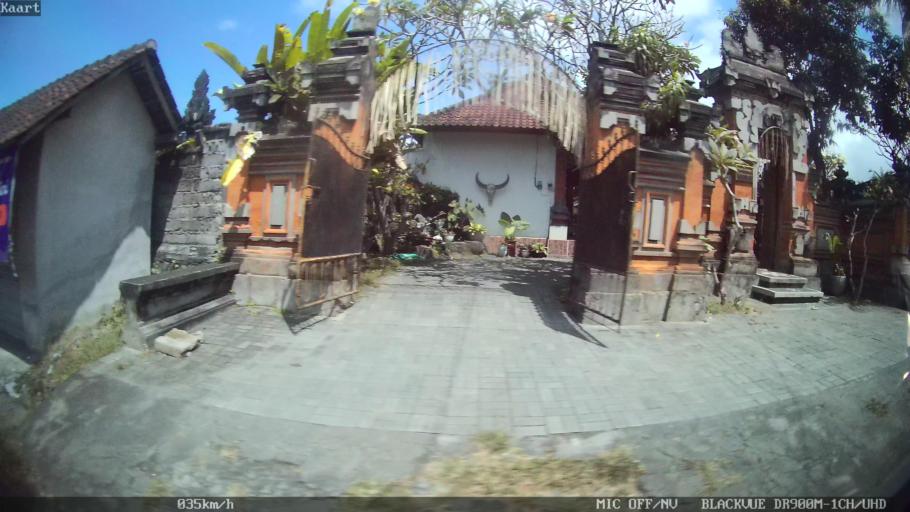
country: ID
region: Bali
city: Banjar Pasekan
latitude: -8.6005
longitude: 115.3089
